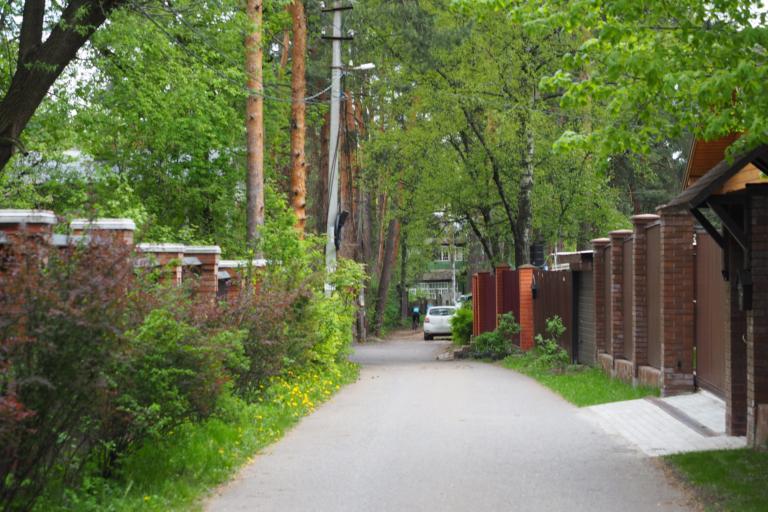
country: RU
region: Moskovskaya
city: Kratovo
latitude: 55.5837
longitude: 38.1666
